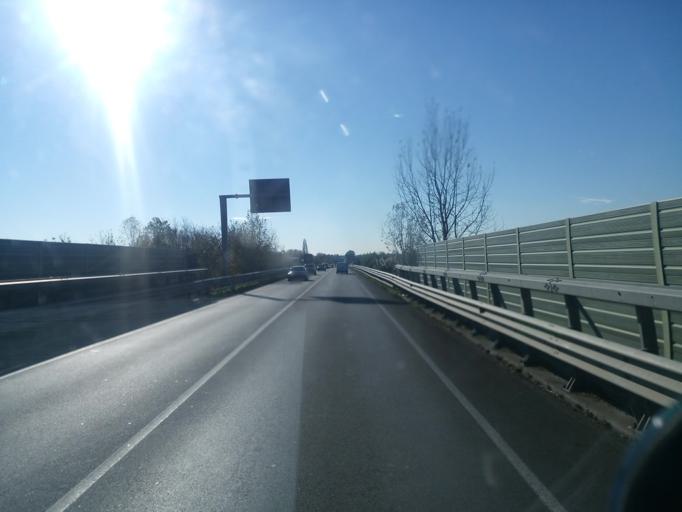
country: IT
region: Veneto
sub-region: Provincia di Padova
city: Borgoricco-San Michele delle Badesse-Sant'Eufemia
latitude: 45.5351
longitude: 11.9440
